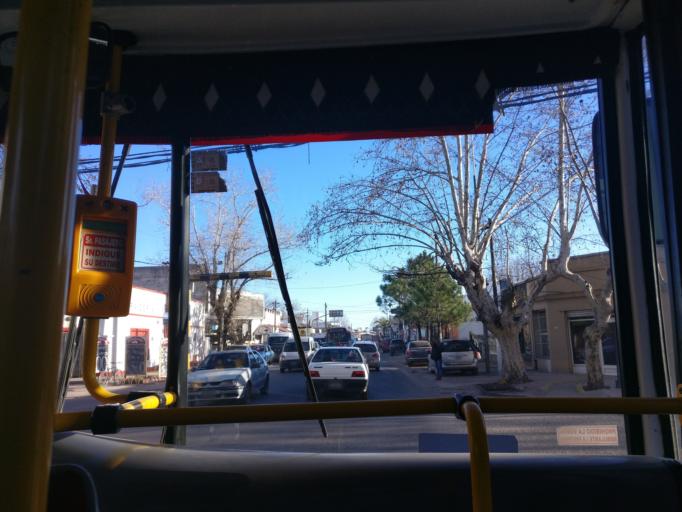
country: AR
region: Buenos Aires
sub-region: Partido de Ezeiza
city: Ezeiza
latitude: -34.8907
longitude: -58.5688
